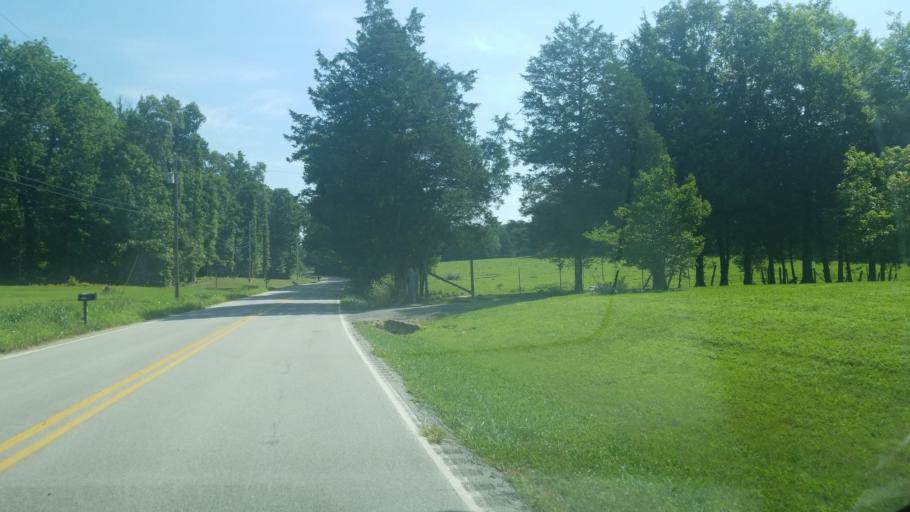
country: US
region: Tennessee
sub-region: Hamilton County
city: Sale Creek
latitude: 35.3492
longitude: -84.9977
